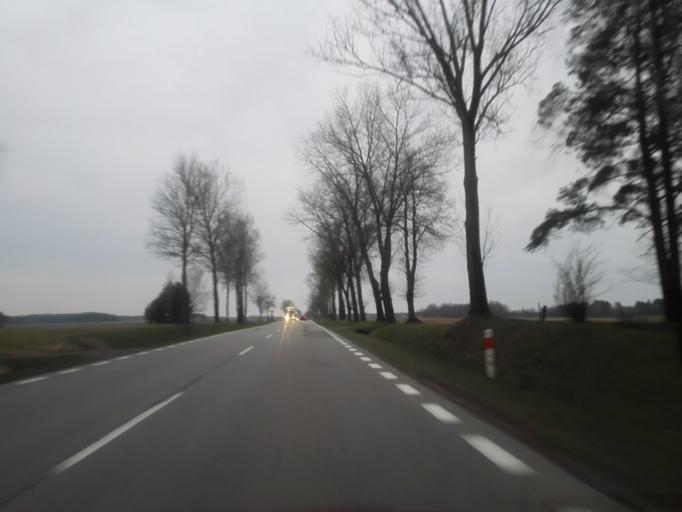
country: PL
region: Podlasie
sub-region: Powiat kolnenski
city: Stawiski
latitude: 53.3085
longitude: 22.1494
